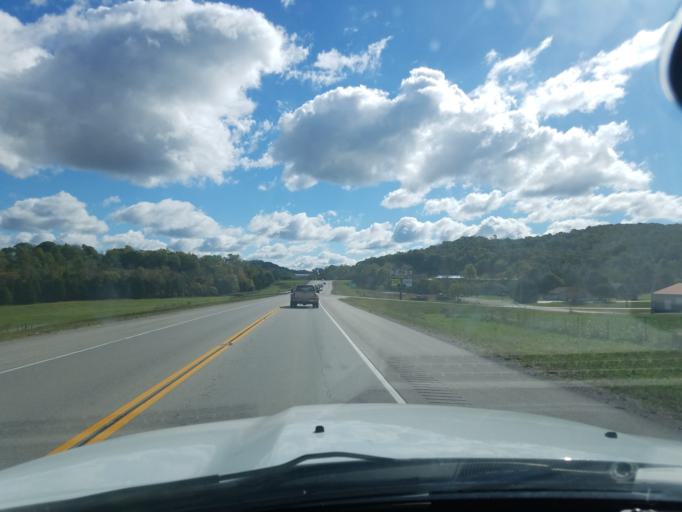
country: US
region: Kentucky
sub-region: Rockcastle County
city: Mount Vernon
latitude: 37.3516
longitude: -84.3776
